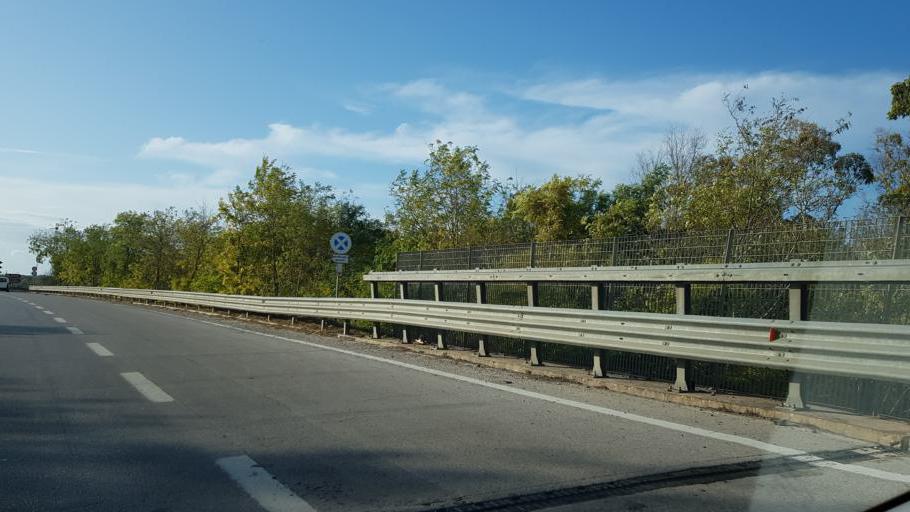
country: IT
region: Apulia
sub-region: Provincia di Brindisi
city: Francavilla Fontana
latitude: 40.5462
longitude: 17.5931
